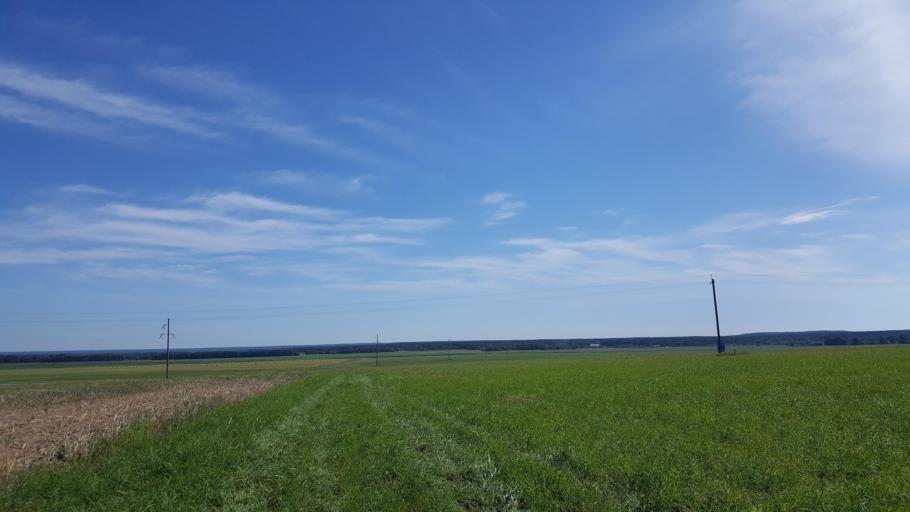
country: BY
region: Brest
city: Kamyanyets
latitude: 52.4038
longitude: 23.8595
